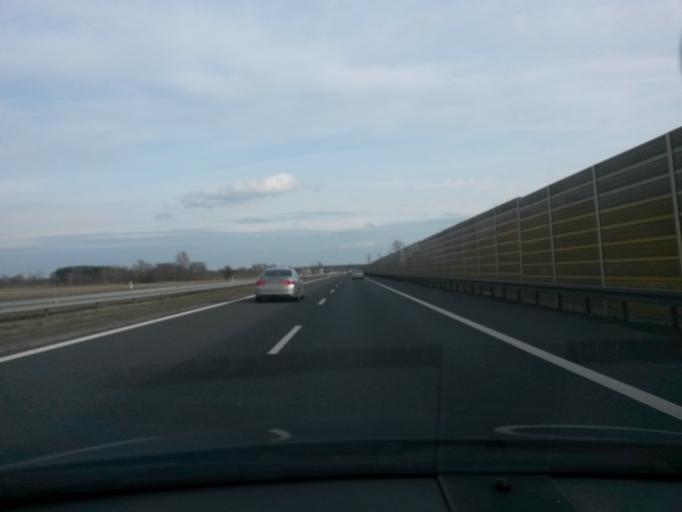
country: PL
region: Greater Poland Voivodeship
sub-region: Powiat kolski
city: Dabie
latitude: 52.0517
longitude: 18.8462
